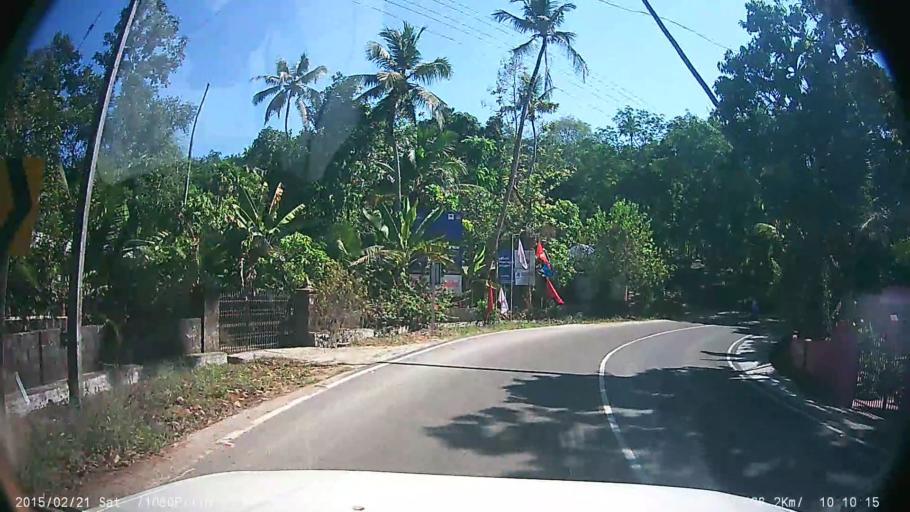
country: IN
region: Kerala
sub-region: Ernakulam
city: Muvattupuzha
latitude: 9.8811
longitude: 76.6133
